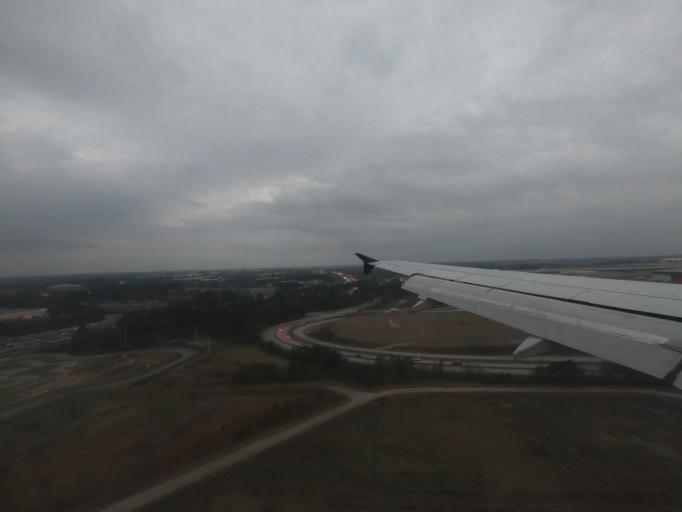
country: US
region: Georgia
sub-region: Fulton County
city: Hapeville
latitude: 33.6495
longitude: -84.4019
